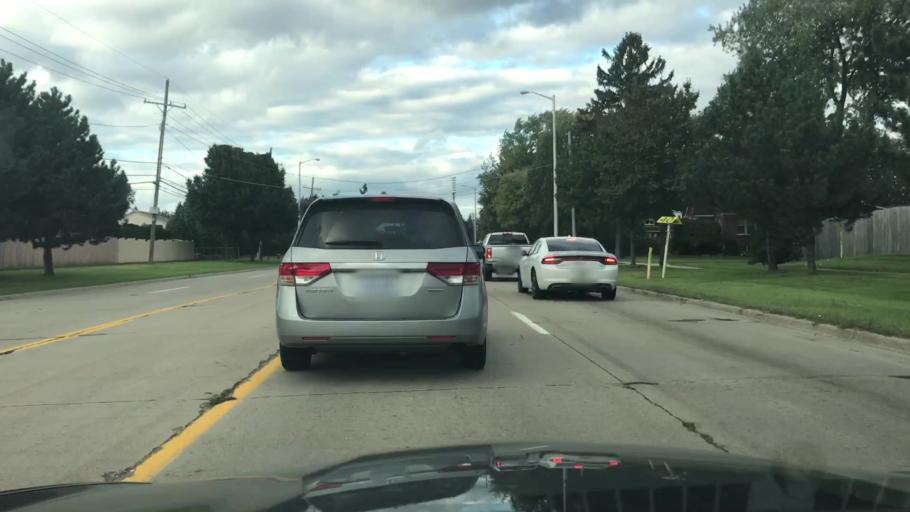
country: US
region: Michigan
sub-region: Macomb County
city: Sterling Heights
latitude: 42.5877
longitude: -83.0705
